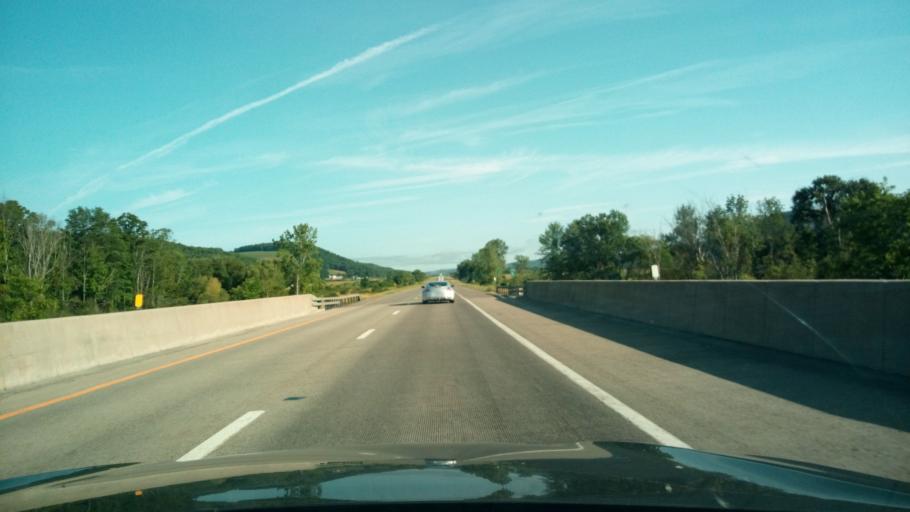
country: US
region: New York
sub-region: Steuben County
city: Wayland
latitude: 42.4494
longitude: -77.4741
